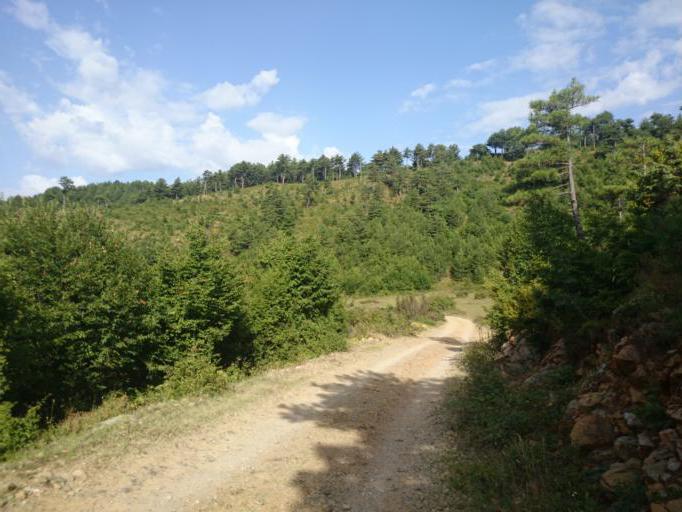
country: AL
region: Elbasan
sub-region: Rrethi i Gramshit
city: Lenias
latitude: 40.7754
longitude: 20.3438
